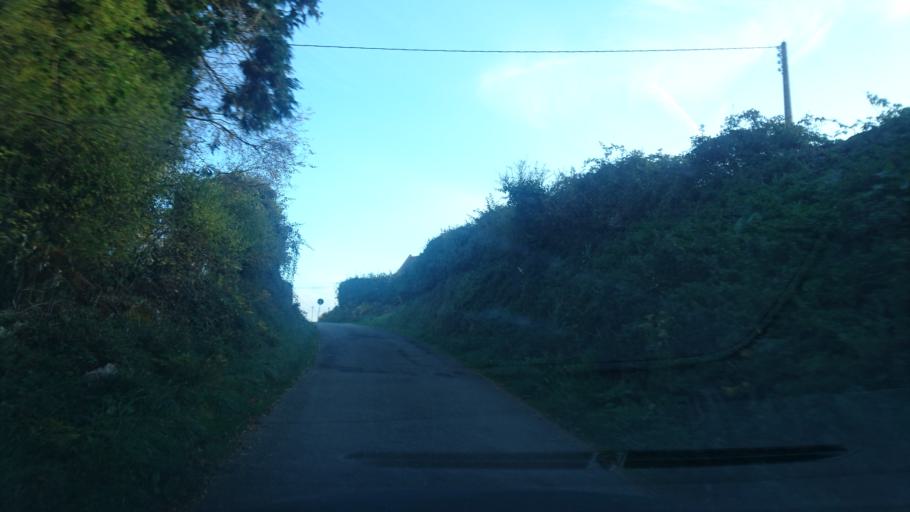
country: FR
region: Brittany
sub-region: Departement du Finistere
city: Lampaul-Plouarzel
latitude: 48.4421
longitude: -4.7684
